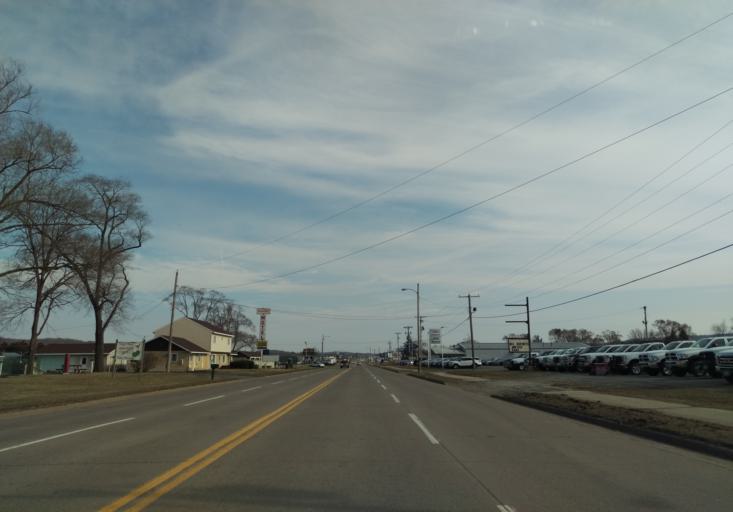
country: US
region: Wisconsin
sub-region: Crawford County
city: Prairie du Chien
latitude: 43.0326
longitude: -91.1343
